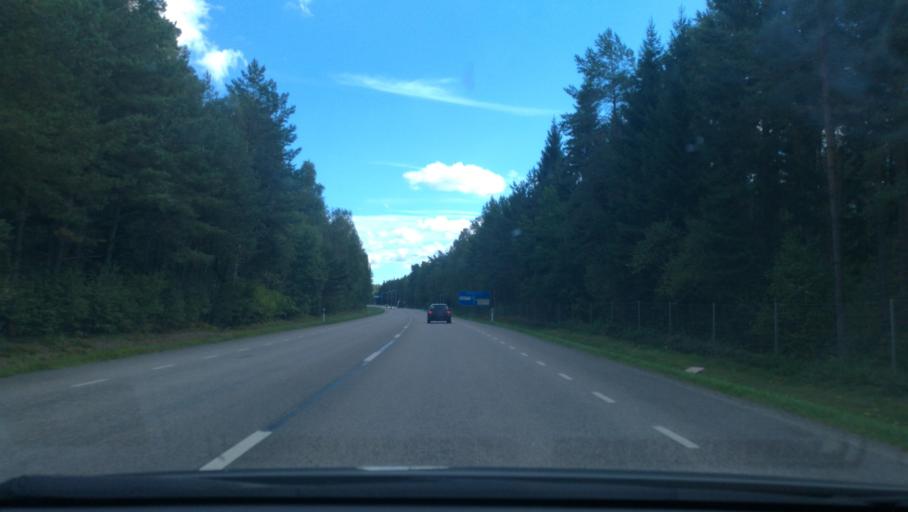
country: SE
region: Vaestra Goetaland
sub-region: Lidkopings Kommun
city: Lidkoping
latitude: 58.4870
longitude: 13.1615
